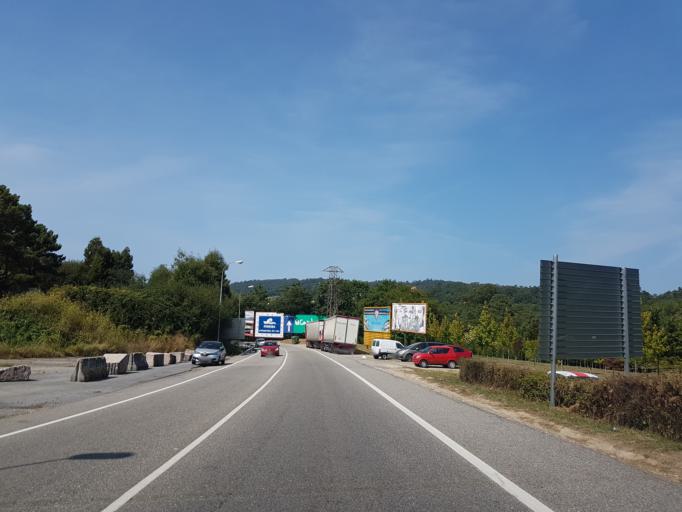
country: ES
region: Galicia
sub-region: Provincia de Pontevedra
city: Redondela
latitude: 42.2244
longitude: -8.6354
